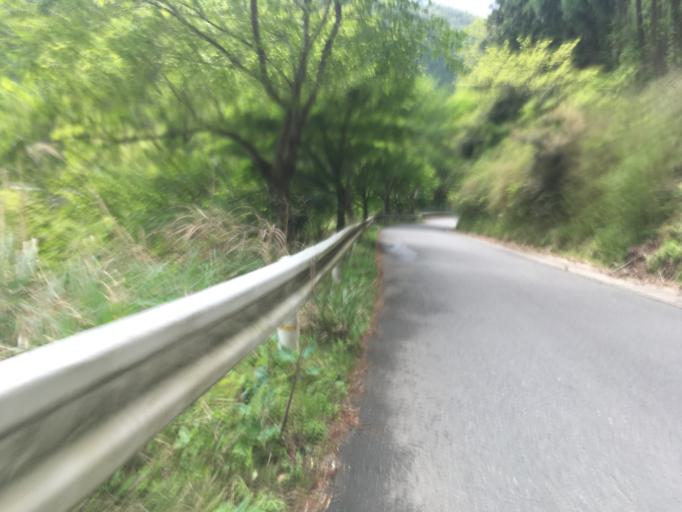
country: JP
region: Kyoto
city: Kameoka
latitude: 35.1403
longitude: 135.5768
